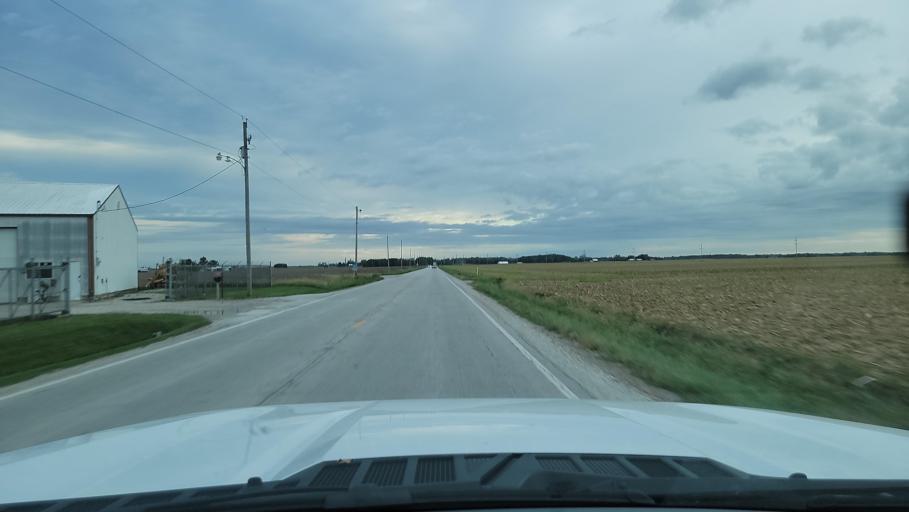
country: US
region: Illinois
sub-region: Schuyler County
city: Rushville
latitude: 40.1380
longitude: -90.5608
